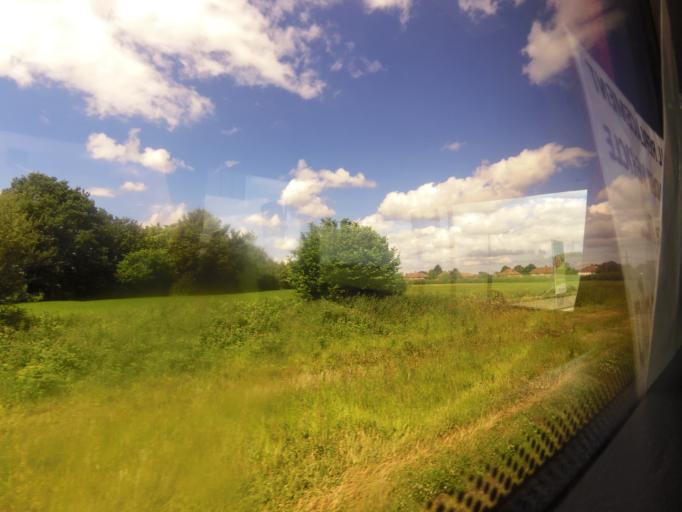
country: GB
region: England
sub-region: Norfolk
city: Aylsham
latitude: 52.7828
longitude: 1.2554
